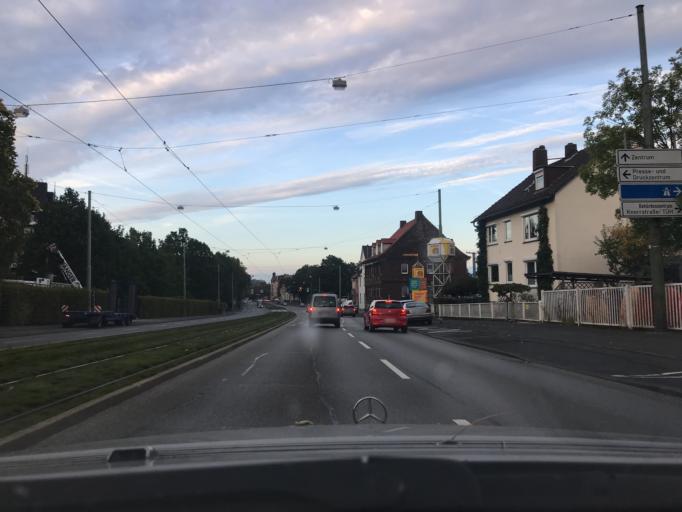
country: DE
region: Hesse
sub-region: Regierungsbezirk Kassel
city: Fuldabruck
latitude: 51.2940
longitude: 9.4770
